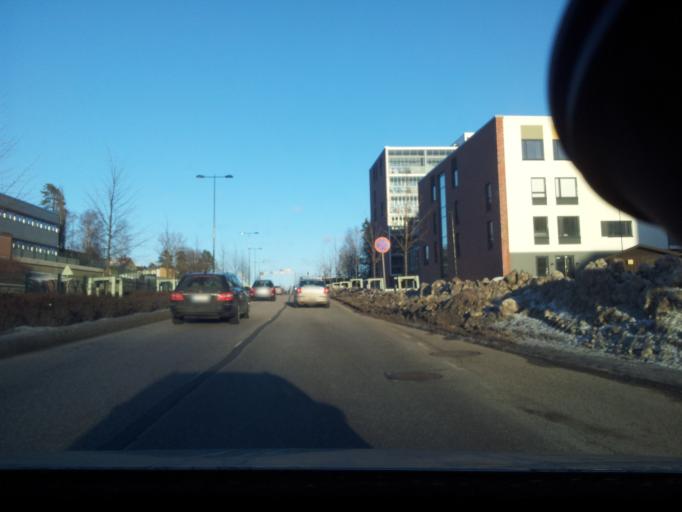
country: FI
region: Uusimaa
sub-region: Helsinki
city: Koukkuniemi
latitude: 60.1667
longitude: 24.7398
